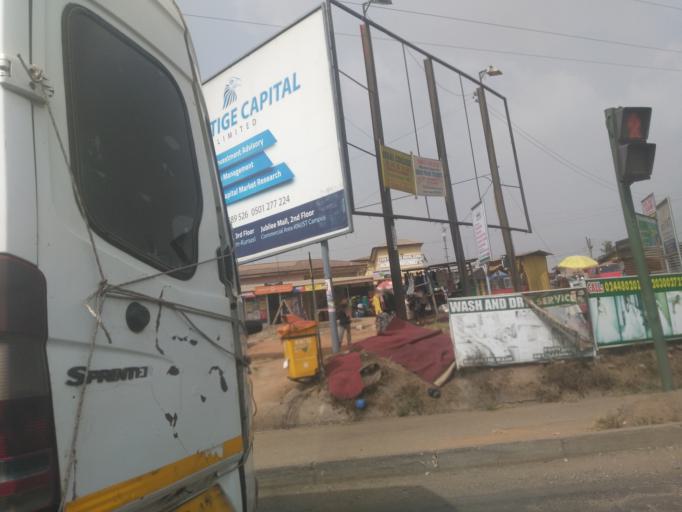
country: GH
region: Ashanti
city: Kumasi
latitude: 6.6873
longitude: -1.5780
